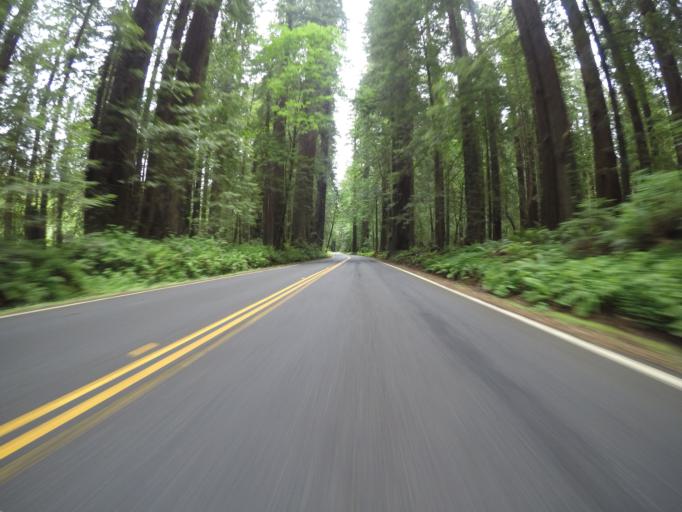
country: US
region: California
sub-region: Humboldt County
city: Rio Dell
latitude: 40.4442
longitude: -124.0194
